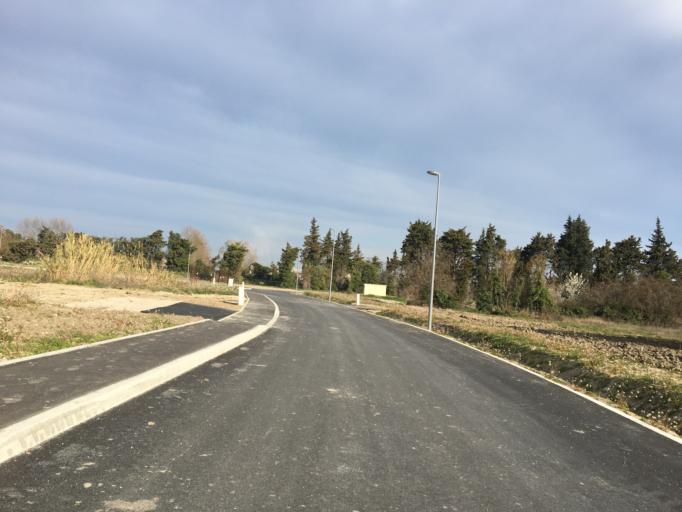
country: FR
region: Provence-Alpes-Cote d'Azur
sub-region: Departement du Vaucluse
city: Le Thor
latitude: 43.9261
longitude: 5.0151
